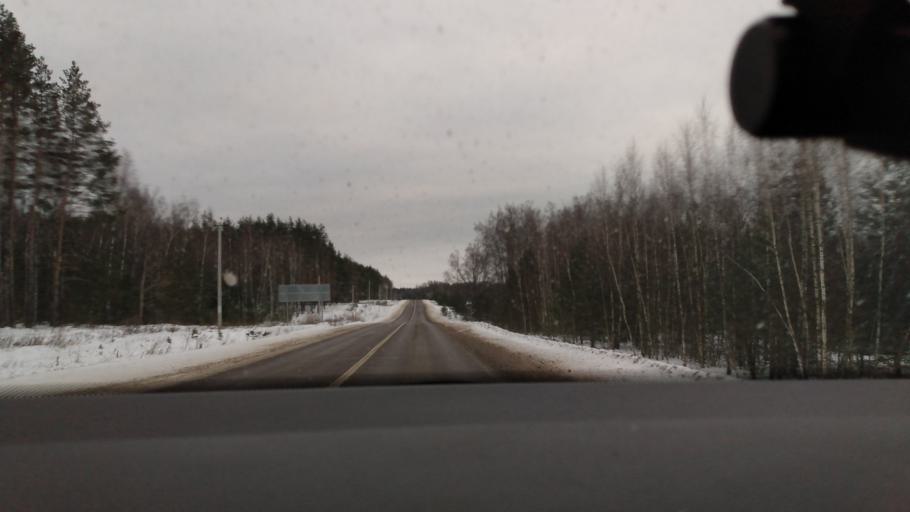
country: RU
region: Moskovskaya
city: Yegor'yevsk
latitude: 55.2508
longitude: 39.0638
